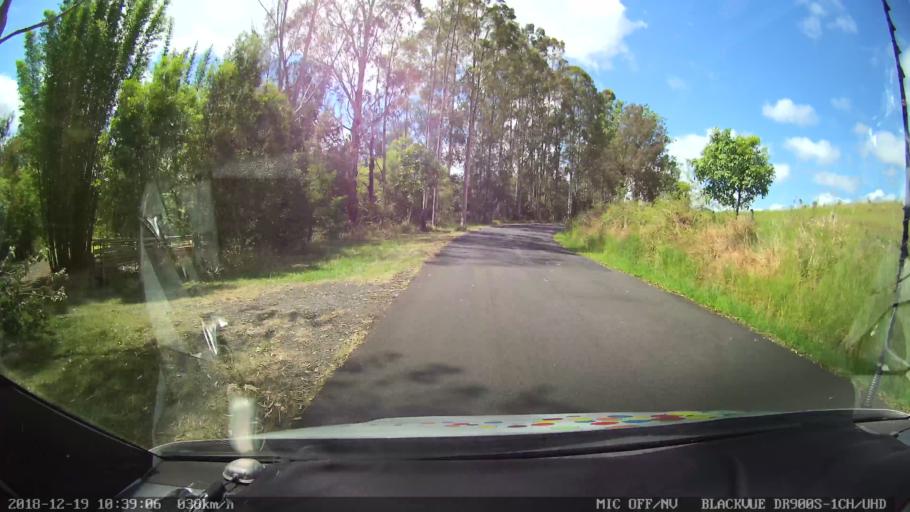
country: AU
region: New South Wales
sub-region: Lismore Municipality
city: Nimbin
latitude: -28.5785
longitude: 153.1544
